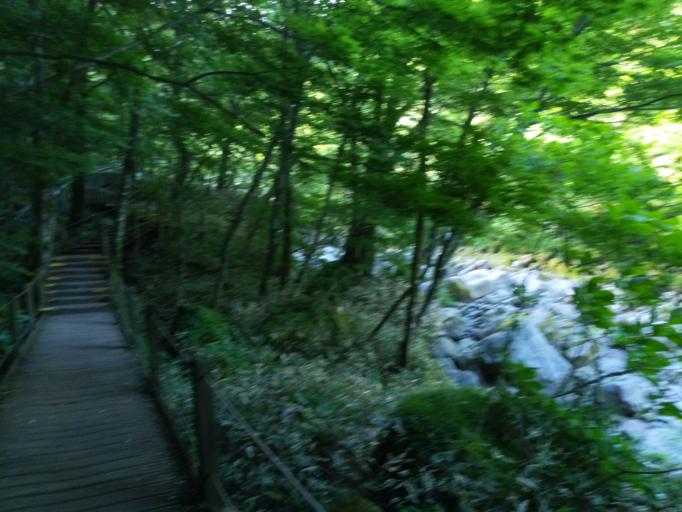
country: KR
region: Jeju-do
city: Jeju-si
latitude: 33.4015
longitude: 126.5399
